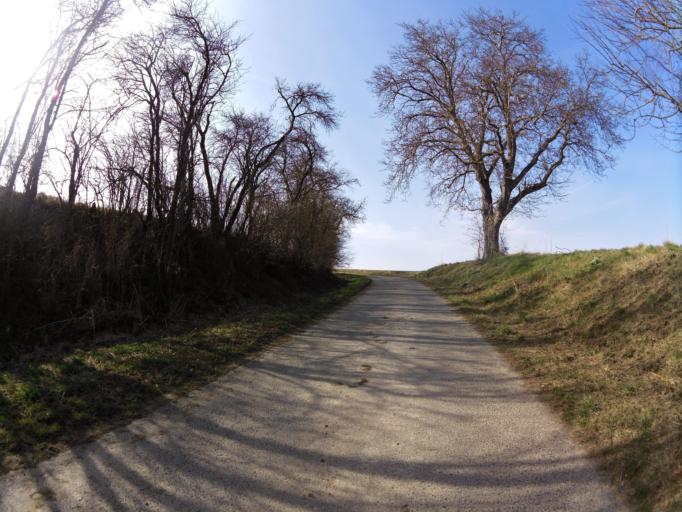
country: DE
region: Bavaria
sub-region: Regierungsbezirk Unterfranken
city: Prosselsheim
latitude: 49.8267
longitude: 10.1191
